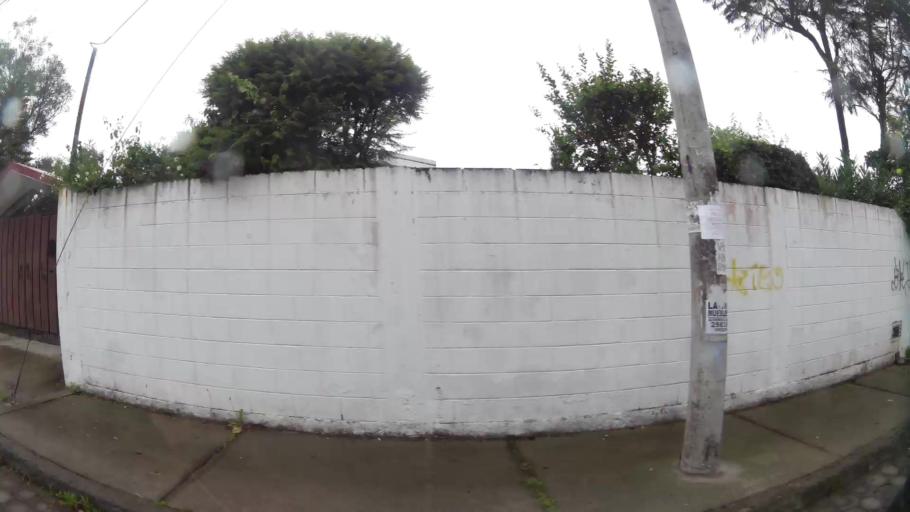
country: EC
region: Pichincha
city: Sangolqui
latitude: -0.2736
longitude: -78.4643
